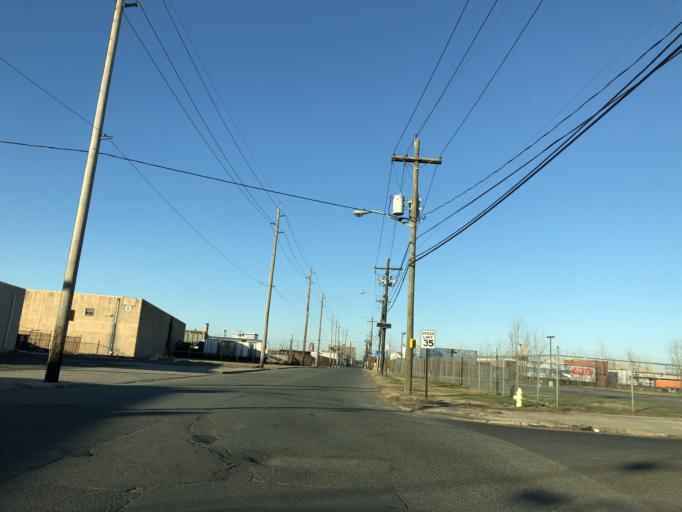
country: US
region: New Jersey
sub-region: Camden County
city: Camden
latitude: 39.9302
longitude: -75.1277
